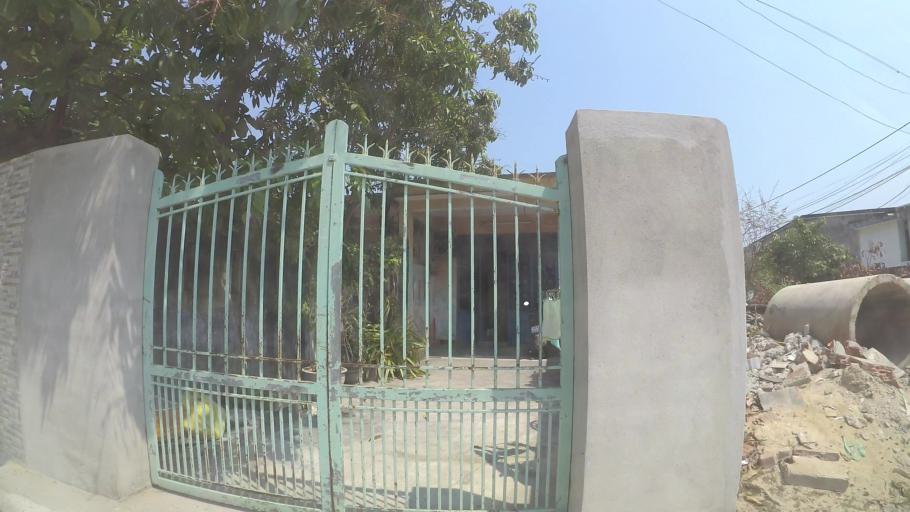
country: VN
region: Da Nang
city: Ngu Hanh Son
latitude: 16.0019
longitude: 108.2644
